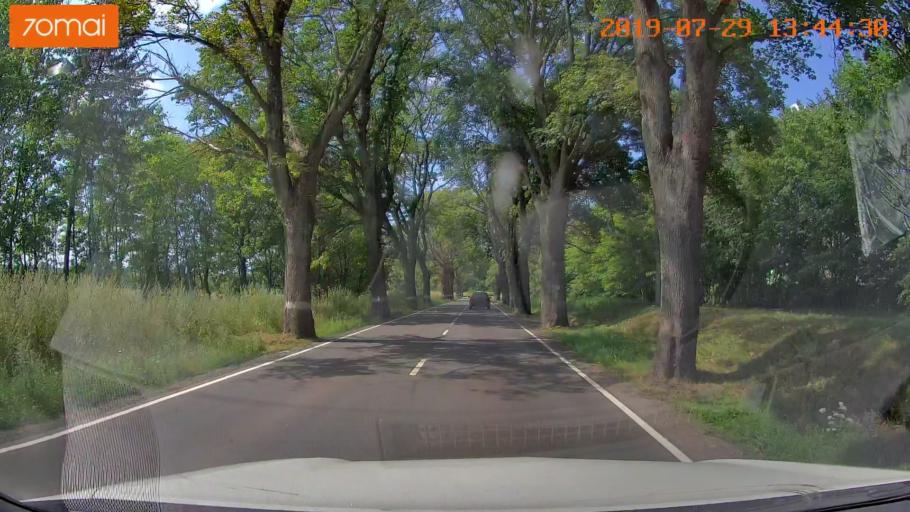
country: RU
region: Kaliningrad
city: Svetlyy
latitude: 54.7378
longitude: 20.0875
